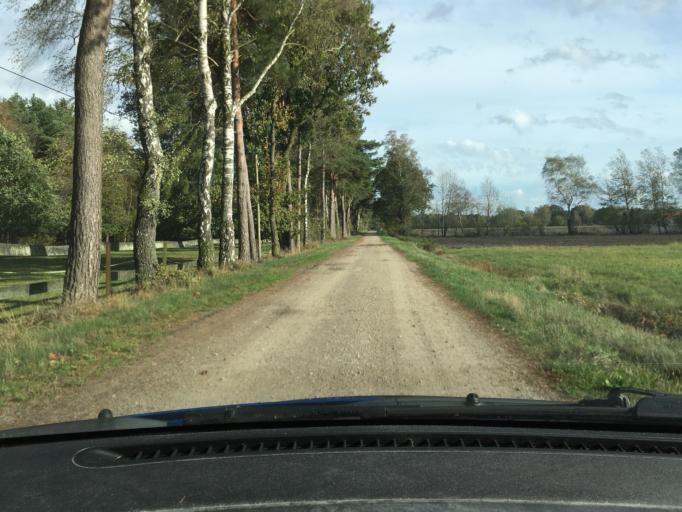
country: DE
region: Lower Saxony
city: Wistedt
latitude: 53.2524
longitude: 9.6403
